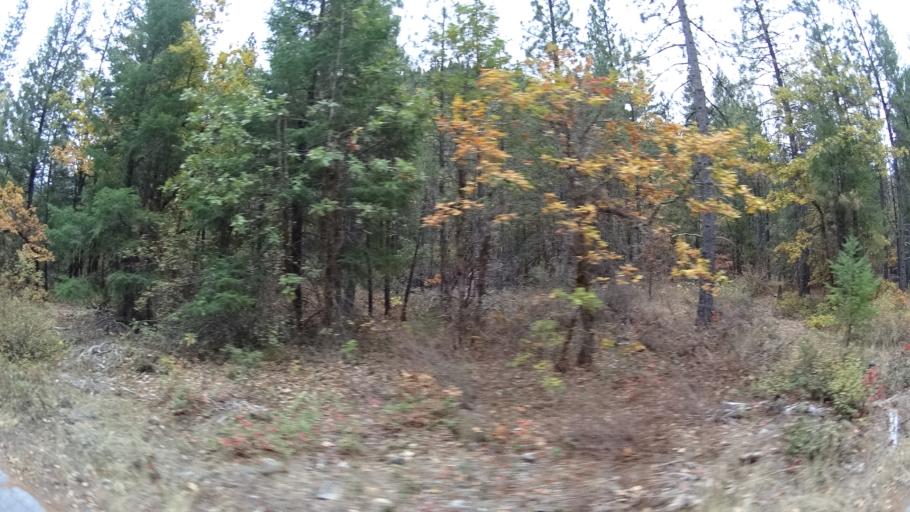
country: US
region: California
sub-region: Siskiyou County
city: Happy Camp
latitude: 41.8805
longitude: -123.4338
